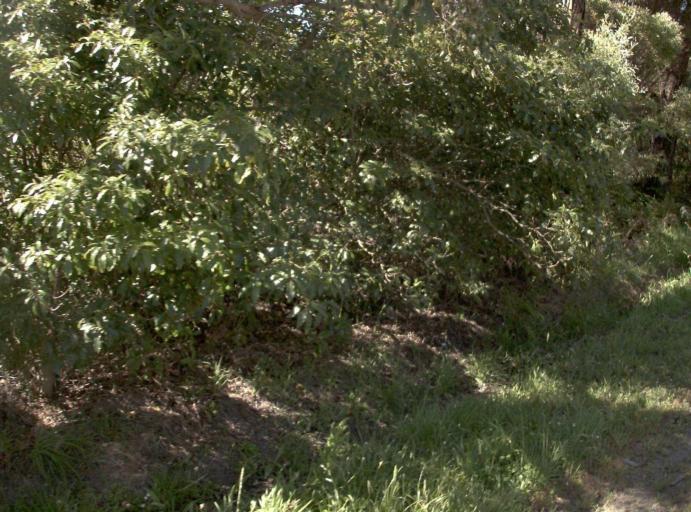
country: AU
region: Victoria
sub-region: Latrobe
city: Morwell
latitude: -38.6672
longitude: 146.4051
